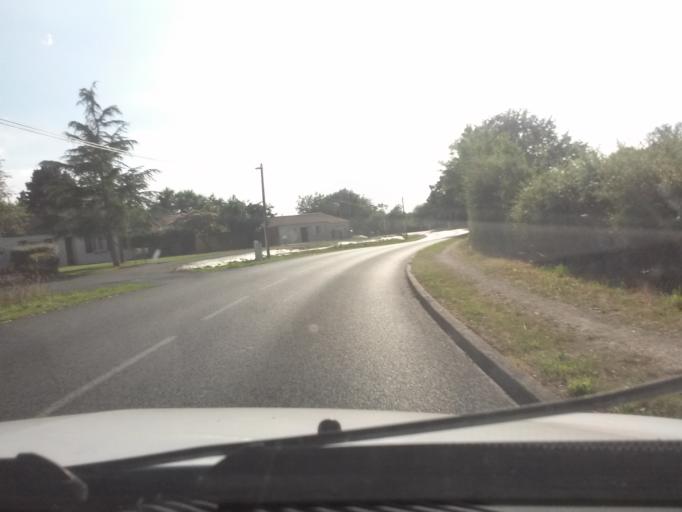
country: FR
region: Pays de la Loire
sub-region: Departement de la Vendee
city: Saint-Hilaire-de-Loulay
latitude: 46.9968
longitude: -1.3415
